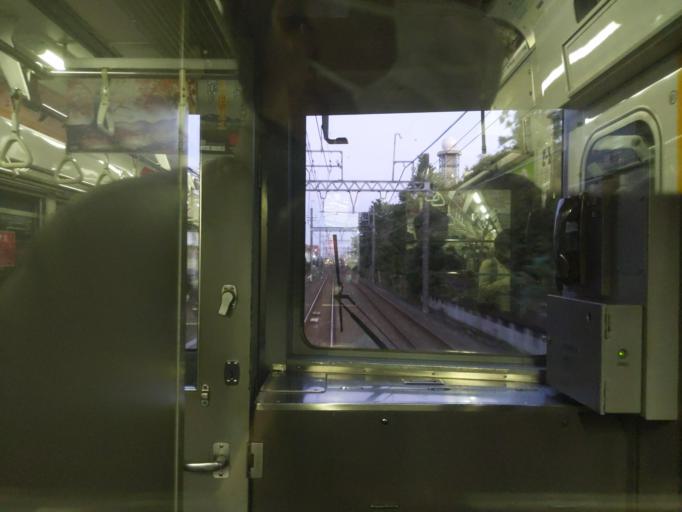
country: JP
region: Chiba
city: Kashiwa
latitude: 35.8609
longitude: 139.9574
